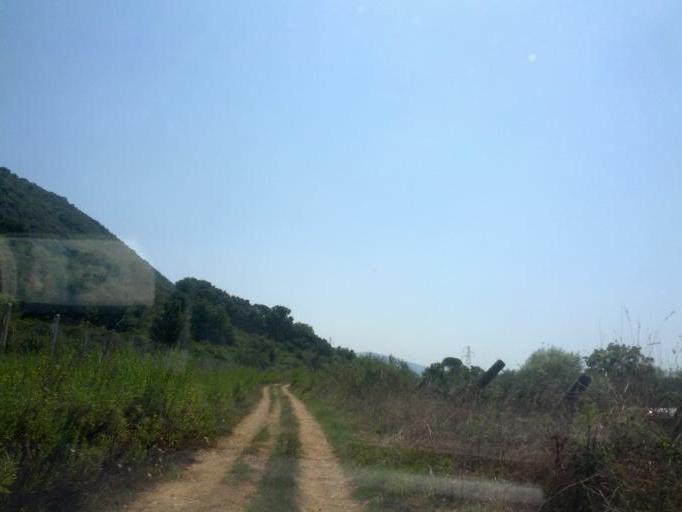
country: IT
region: Latium
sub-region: Provincia di Latina
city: Monte San Biagio
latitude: 41.3657
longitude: 13.3558
